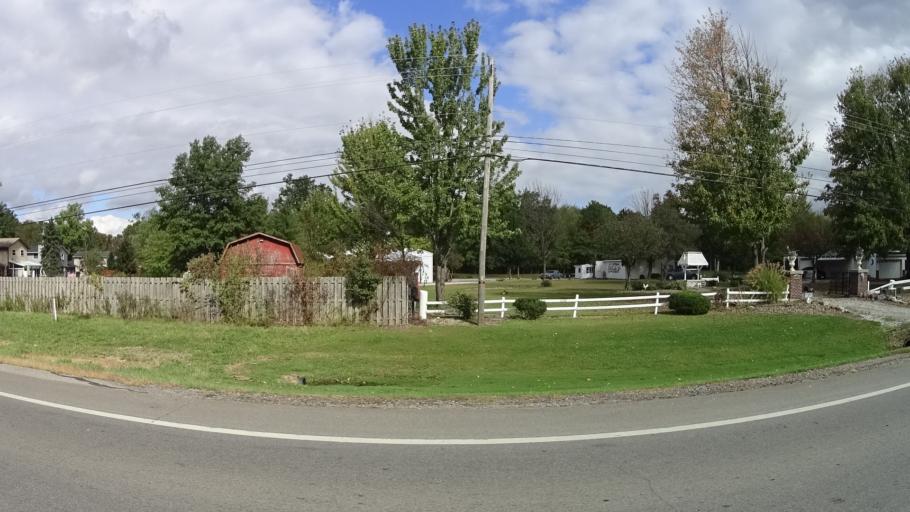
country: US
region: Ohio
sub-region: Lorain County
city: Eaton Estates
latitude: 41.3144
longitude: -82.0262
